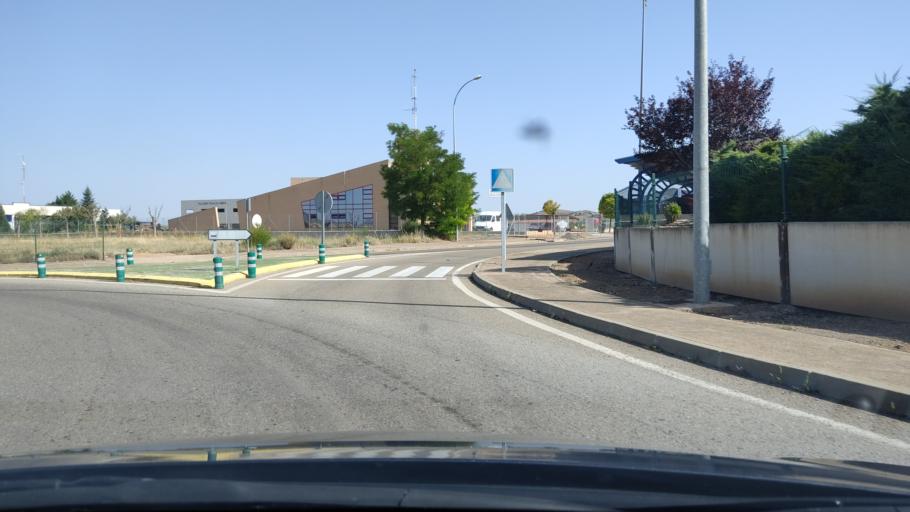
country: ES
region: Aragon
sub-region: Provincia de Teruel
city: Calamocha
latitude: 40.9178
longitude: -1.2832
